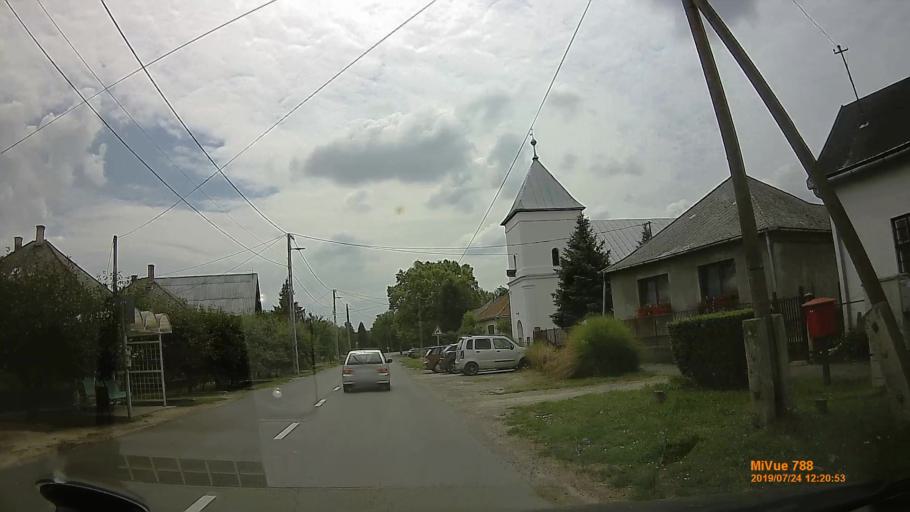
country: HU
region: Szabolcs-Szatmar-Bereg
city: Vasarosnameny
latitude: 48.1327
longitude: 22.3434
